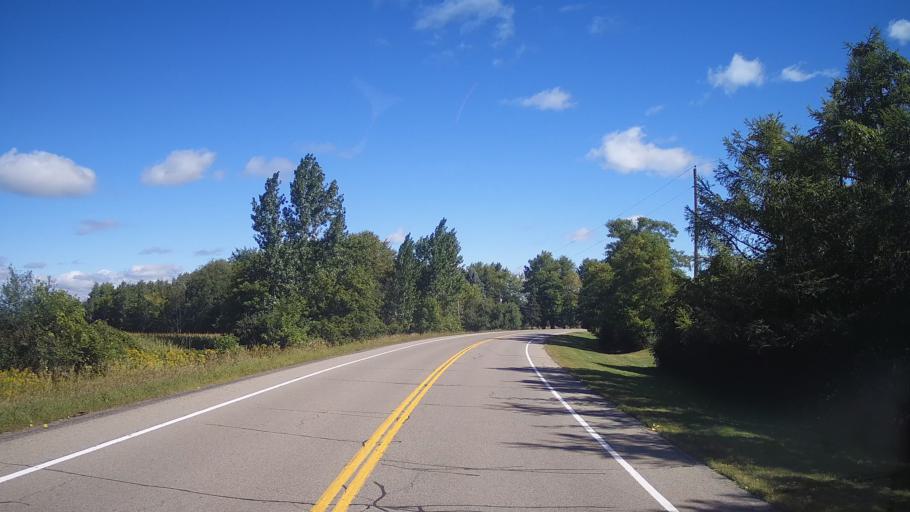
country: US
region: New York
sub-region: St. Lawrence County
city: Norfolk
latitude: 44.9614
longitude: -75.2827
